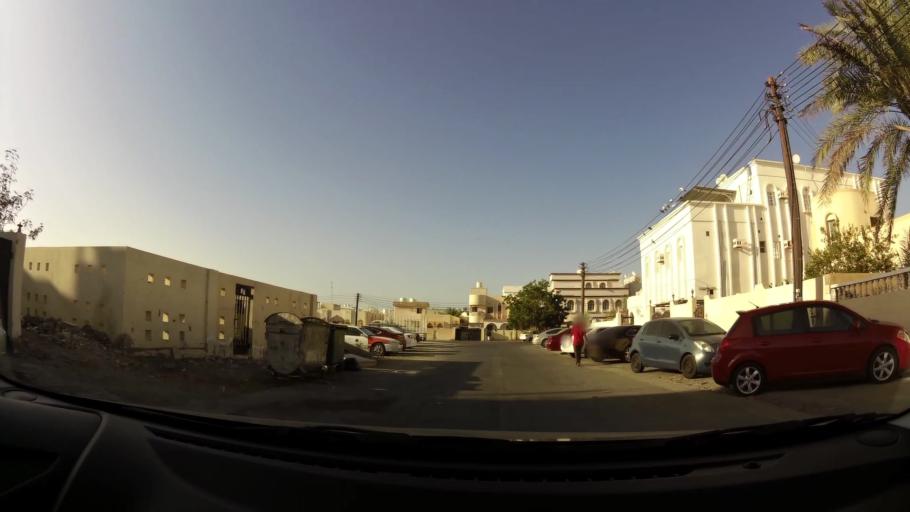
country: OM
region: Muhafazat Masqat
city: As Sib al Jadidah
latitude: 23.6333
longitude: 58.1985
